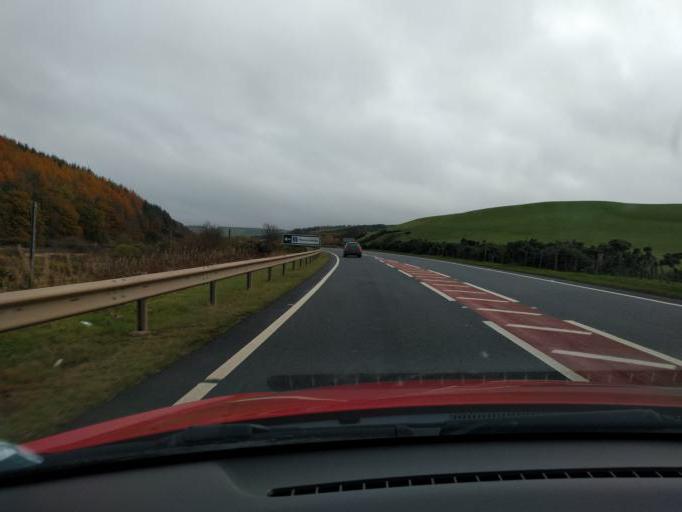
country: GB
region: Scotland
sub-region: The Scottish Borders
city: Duns
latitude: 55.8935
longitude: -2.3293
